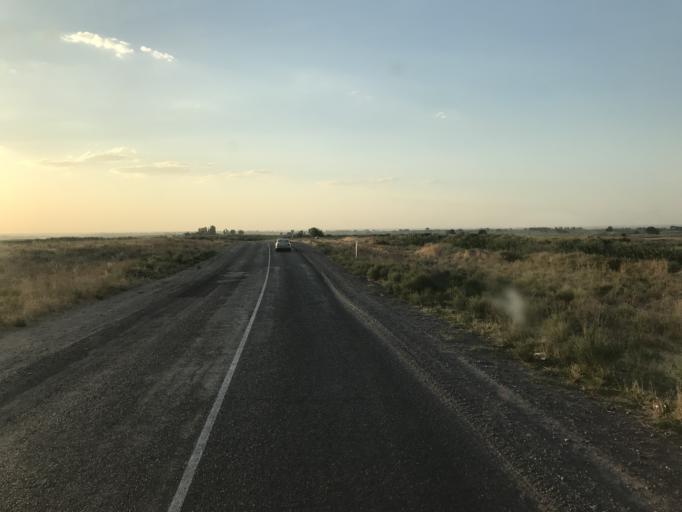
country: UZ
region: Toshkent
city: Yangiyul
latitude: 41.3408
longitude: 68.8784
